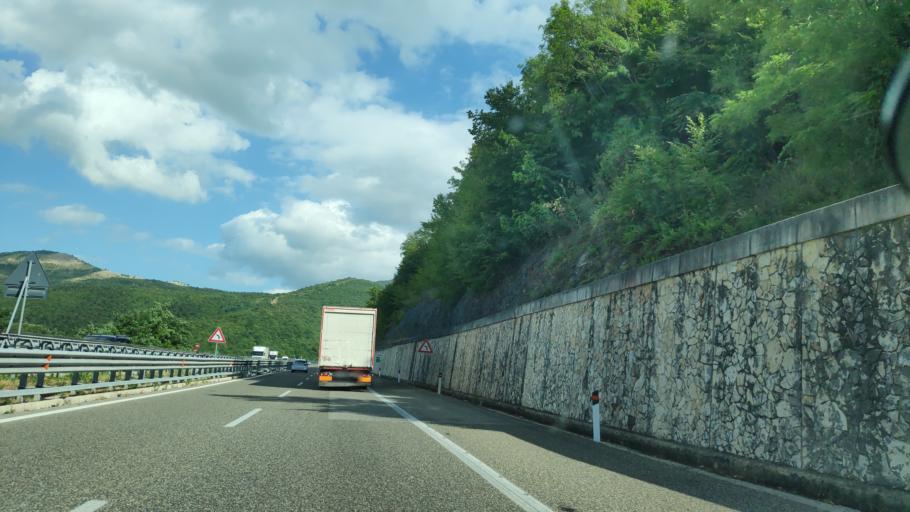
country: IT
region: Campania
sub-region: Provincia di Salerno
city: Pertosa
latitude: 40.5325
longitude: 15.4254
